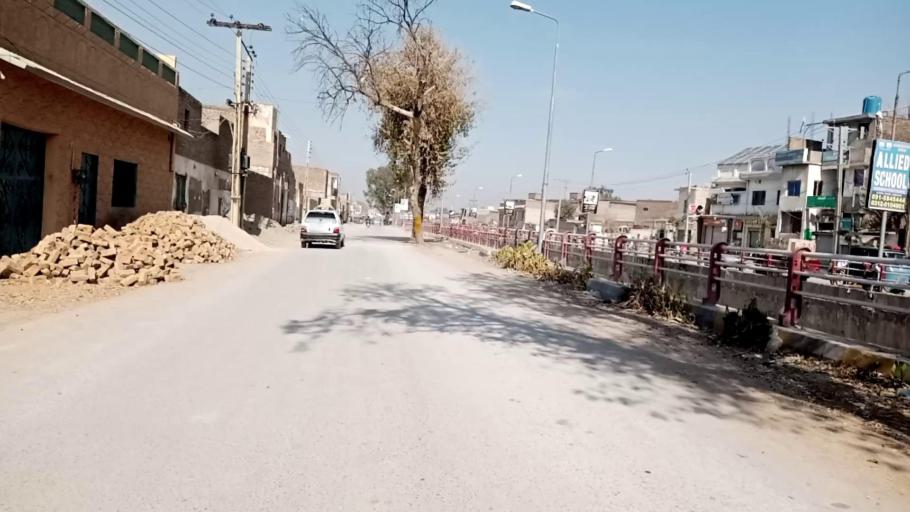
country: PK
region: Khyber Pakhtunkhwa
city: Peshawar
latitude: 33.9835
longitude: 71.4995
